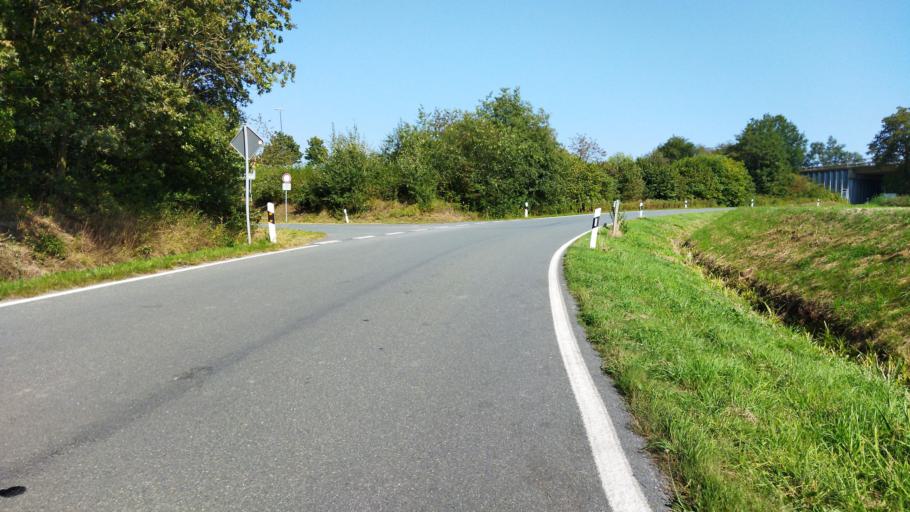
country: DE
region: North Rhine-Westphalia
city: Lengerich
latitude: 52.2288
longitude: 7.8742
